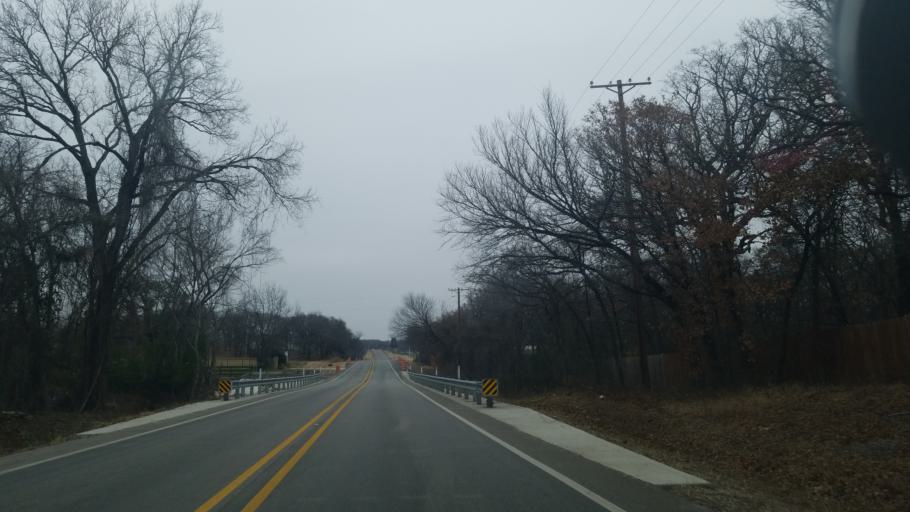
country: US
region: Texas
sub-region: Denton County
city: Argyle
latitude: 33.1205
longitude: -97.1397
